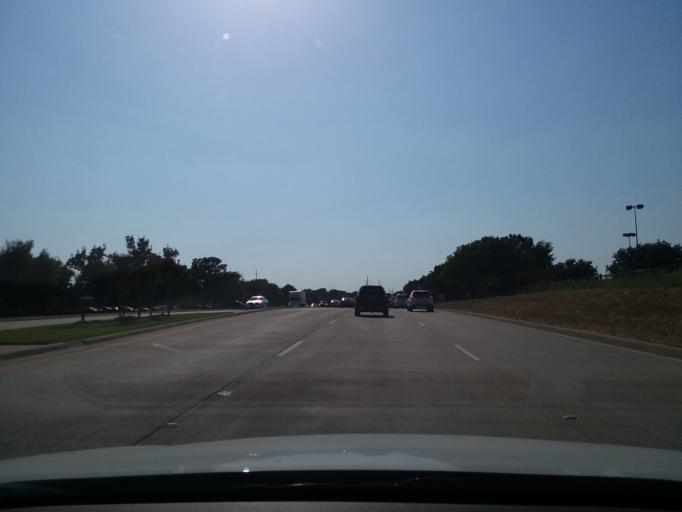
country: US
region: Texas
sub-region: Denton County
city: Flower Mound
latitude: 33.0138
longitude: -97.0672
